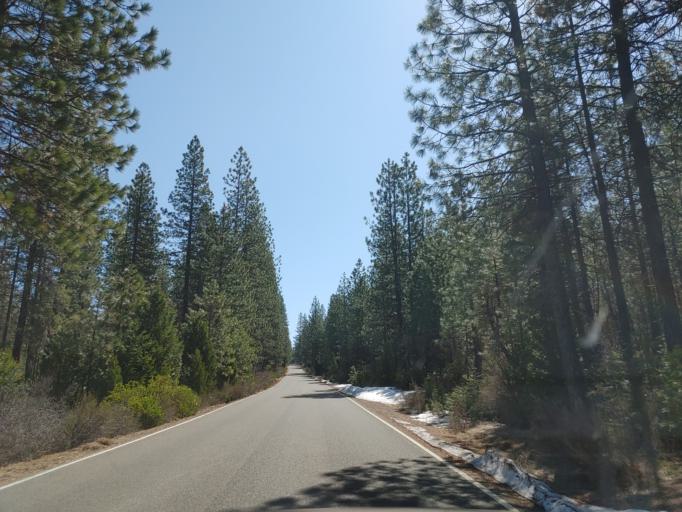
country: US
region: California
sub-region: Siskiyou County
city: McCloud
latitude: 41.2475
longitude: -122.0232
